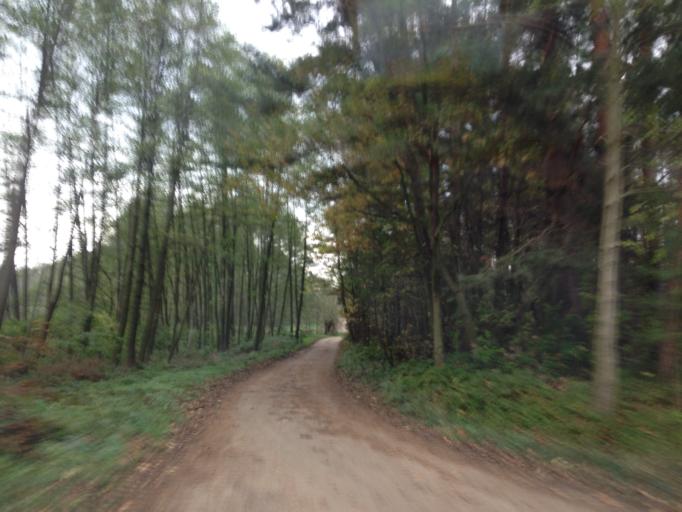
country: PL
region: Kujawsko-Pomorskie
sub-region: Powiat brodnicki
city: Brzozie
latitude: 53.2992
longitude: 19.5565
